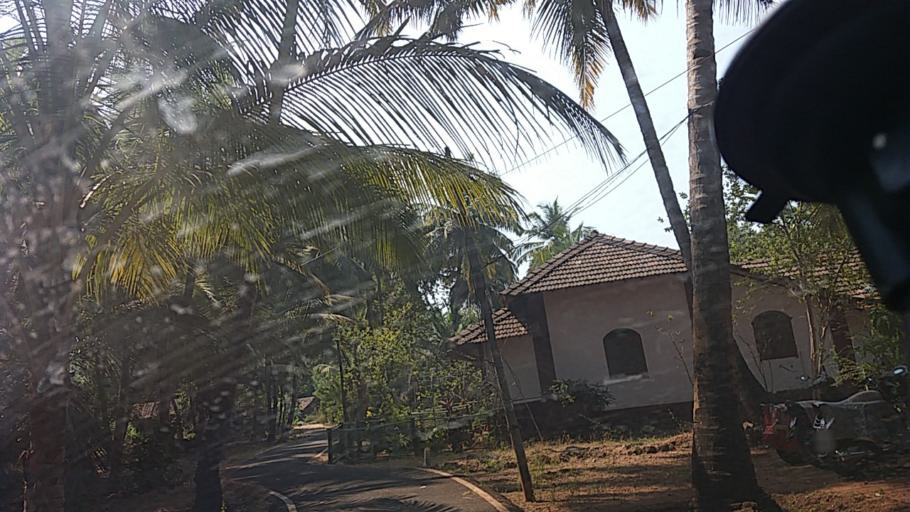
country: IN
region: Goa
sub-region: South Goa
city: Sancoale
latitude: 15.3386
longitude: 73.8966
